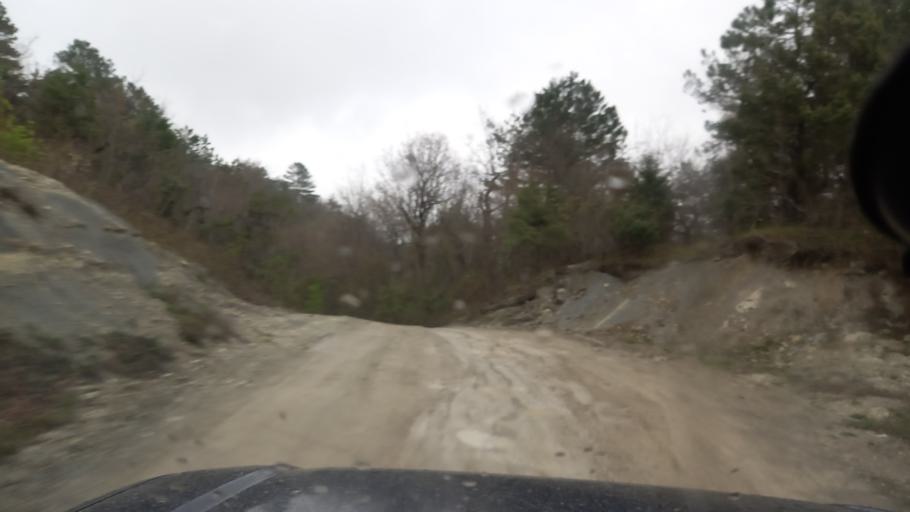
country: RU
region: Krasnodarskiy
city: Dzhubga
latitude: 44.3214
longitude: 38.6809
